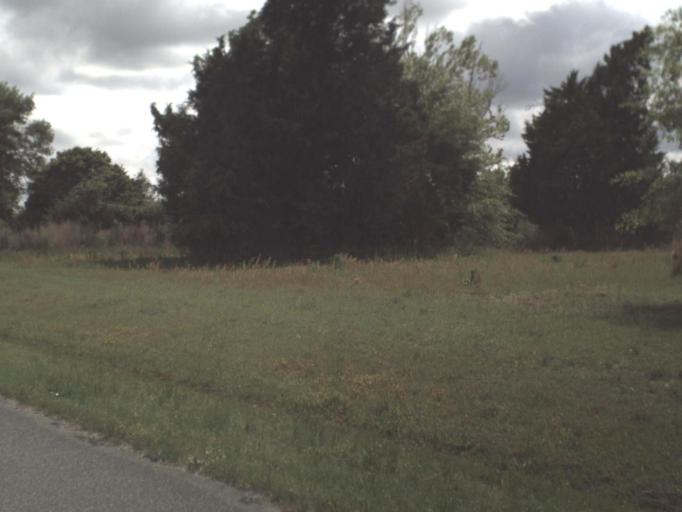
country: US
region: Florida
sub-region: Santa Rosa County
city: Point Baker
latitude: 30.7693
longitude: -87.0929
